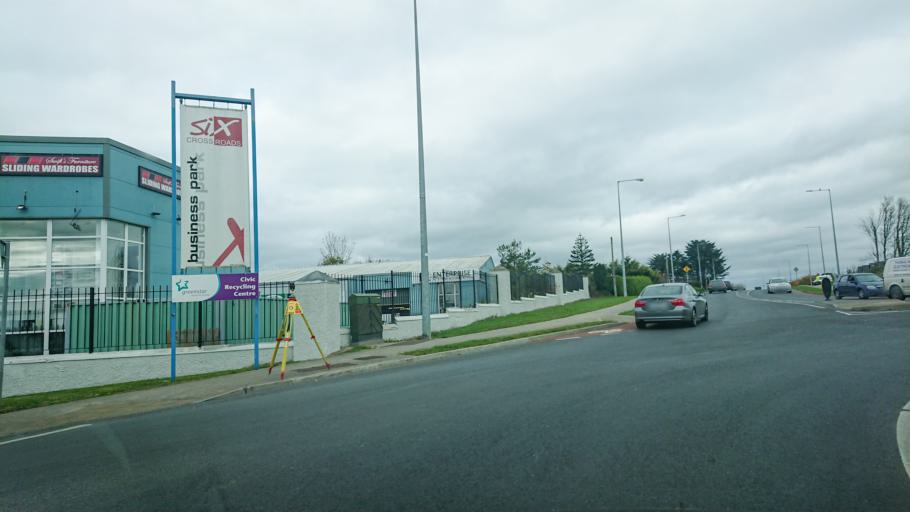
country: IE
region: Munster
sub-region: Waterford
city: Waterford
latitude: 52.2327
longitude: -7.1423
